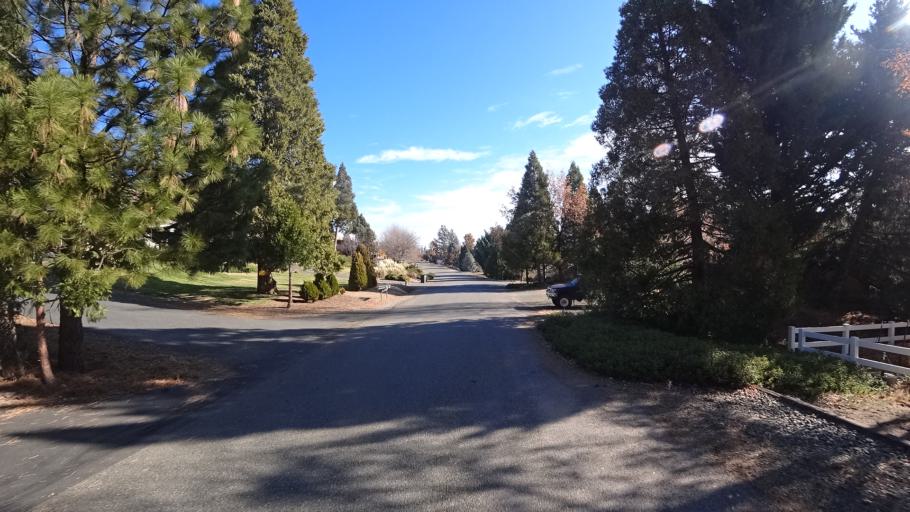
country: US
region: California
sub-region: Siskiyou County
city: Yreka
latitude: 41.6926
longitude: -122.6549
